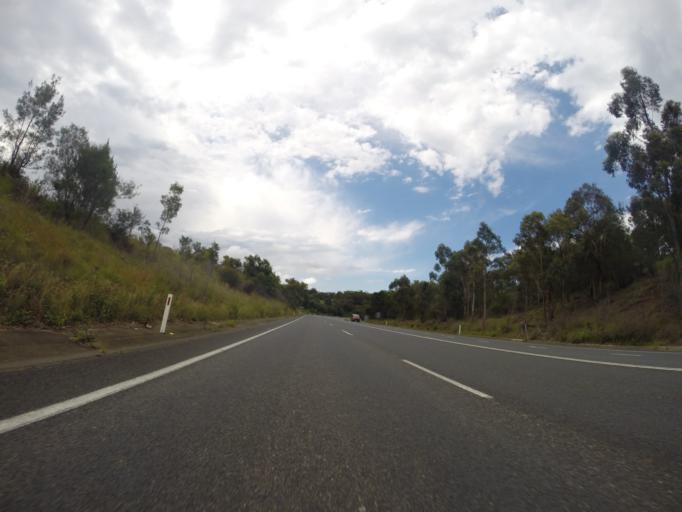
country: AU
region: New South Wales
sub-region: Shoalhaven Shire
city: Milton
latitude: -35.2519
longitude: 150.4235
